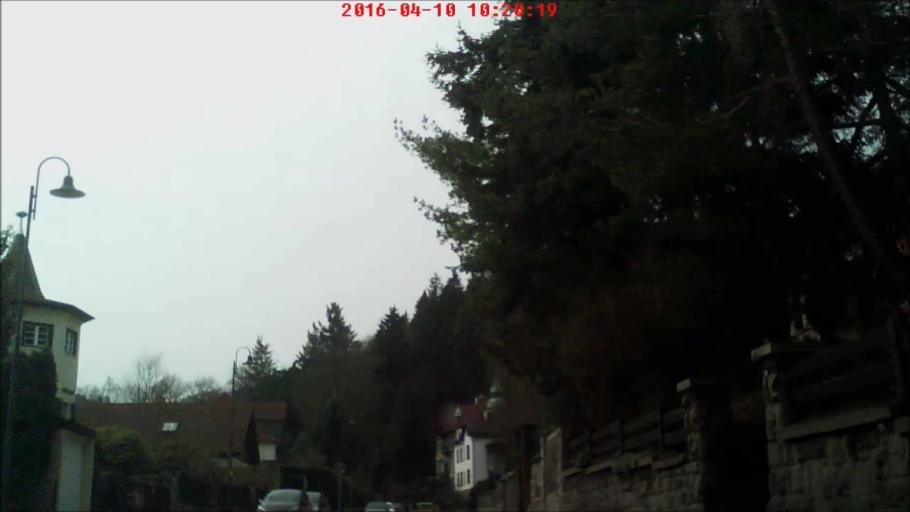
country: DE
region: Thuringia
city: Ilmenau
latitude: 50.6792
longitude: 10.9072
